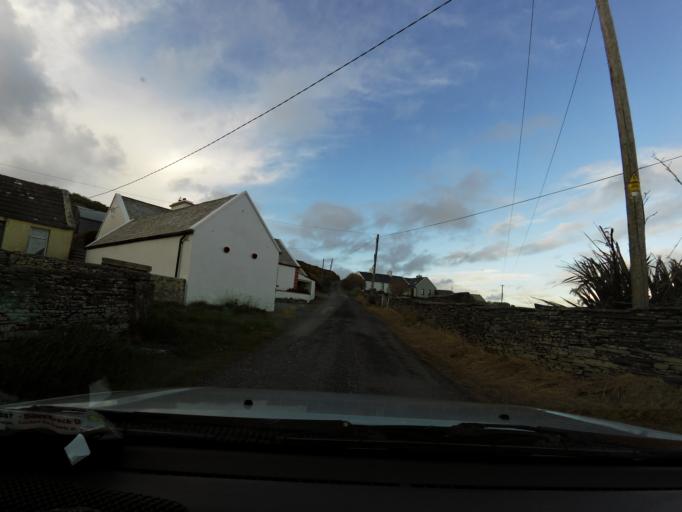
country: IE
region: Munster
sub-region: An Clar
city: Kilrush
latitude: 52.9433
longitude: -9.4509
